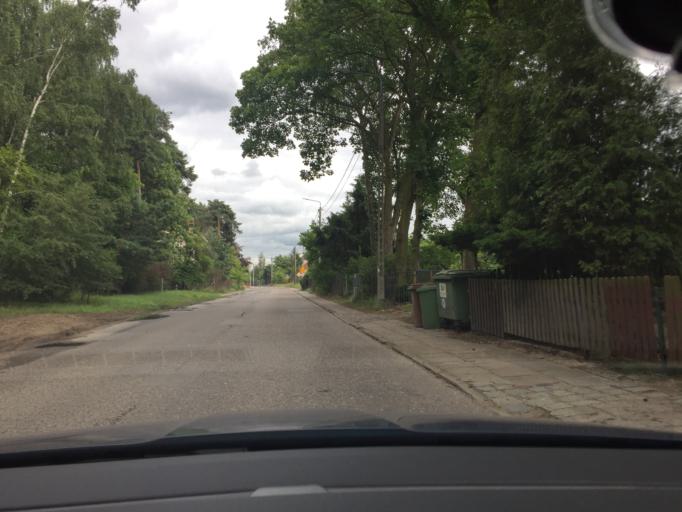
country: PL
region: Pomeranian Voivodeship
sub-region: Gdansk
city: Gdansk
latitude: 54.3608
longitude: 18.7351
